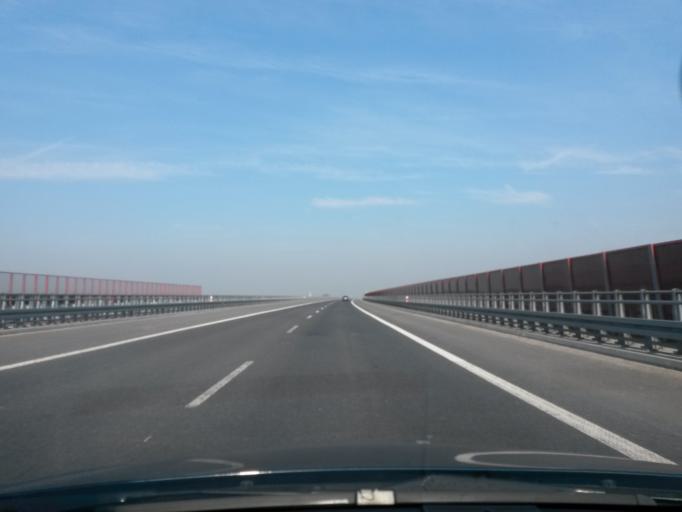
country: PL
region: Lodz Voivodeship
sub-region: Powiat kutnowski
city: Krzyzanow
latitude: 52.1313
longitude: 19.4897
